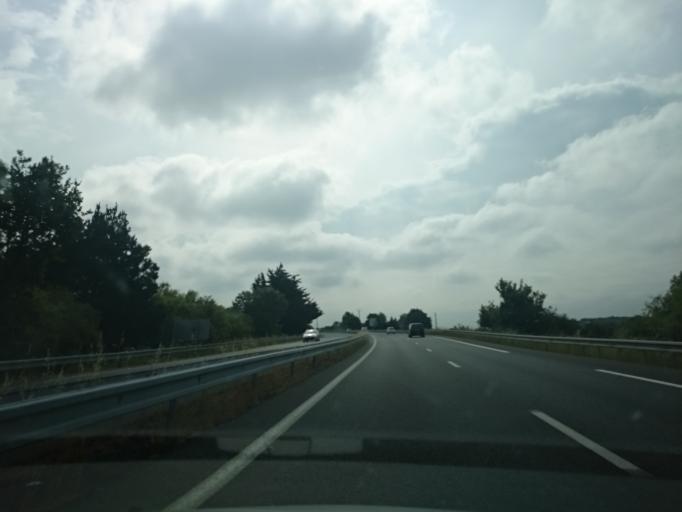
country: FR
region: Brittany
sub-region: Departement du Morbihan
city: Muzillac
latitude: 47.5501
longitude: -2.4825
